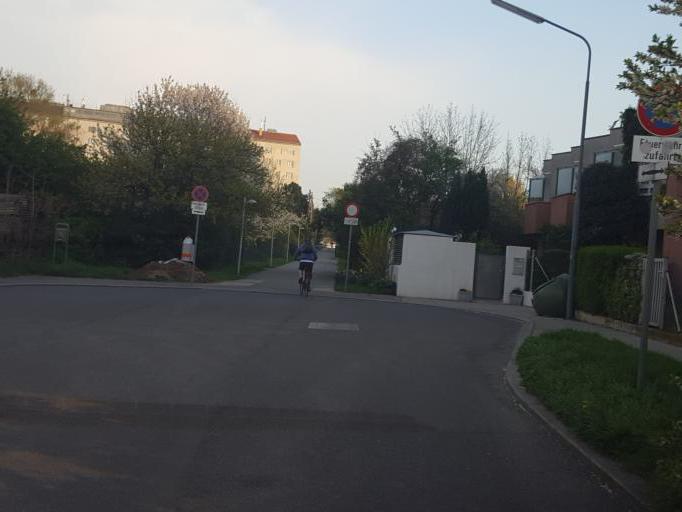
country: AT
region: Lower Austria
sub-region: Politischer Bezirk Wien-Umgebung
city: Schwechat
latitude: 48.1636
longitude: 16.4234
